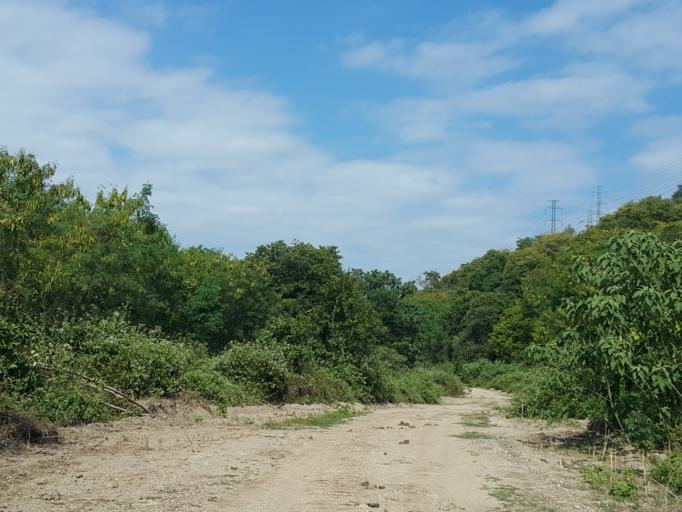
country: TH
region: Lampang
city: Mae Mo
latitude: 18.3284
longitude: 99.7648
